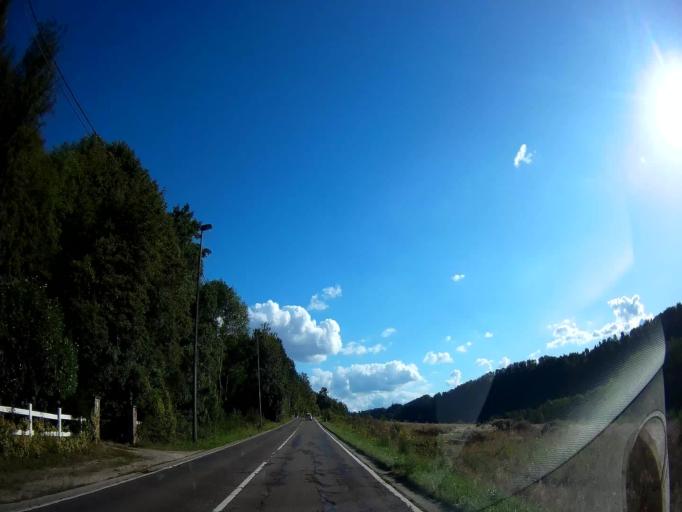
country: BE
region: Wallonia
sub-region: Province de Namur
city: Anhee
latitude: 50.2913
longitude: 4.8968
